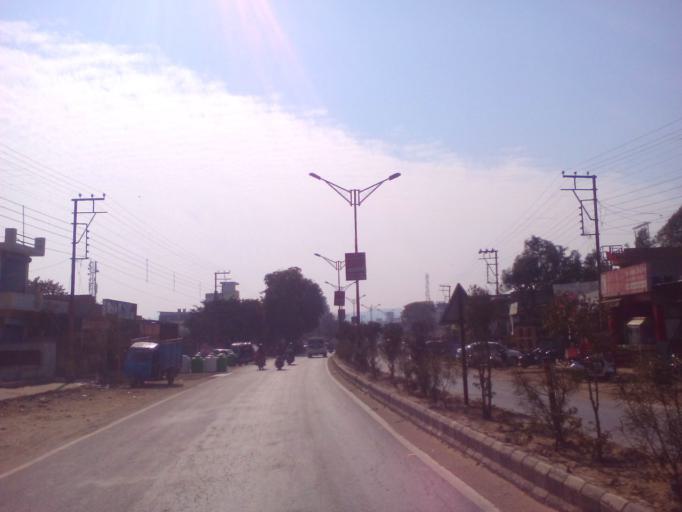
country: IN
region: Uttarakhand
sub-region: Dehradun
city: Clement Town
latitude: 30.2802
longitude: 77.9916
